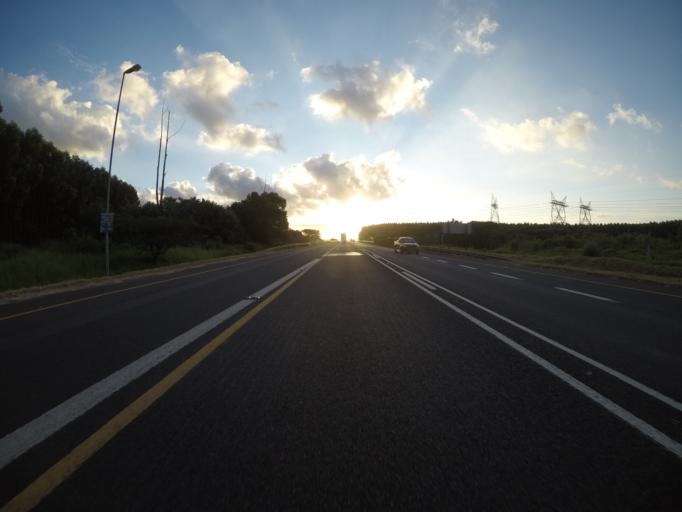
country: ZA
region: KwaZulu-Natal
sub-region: uThungulu District Municipality
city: Richards Bay
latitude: -28.6949
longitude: 32.0245
